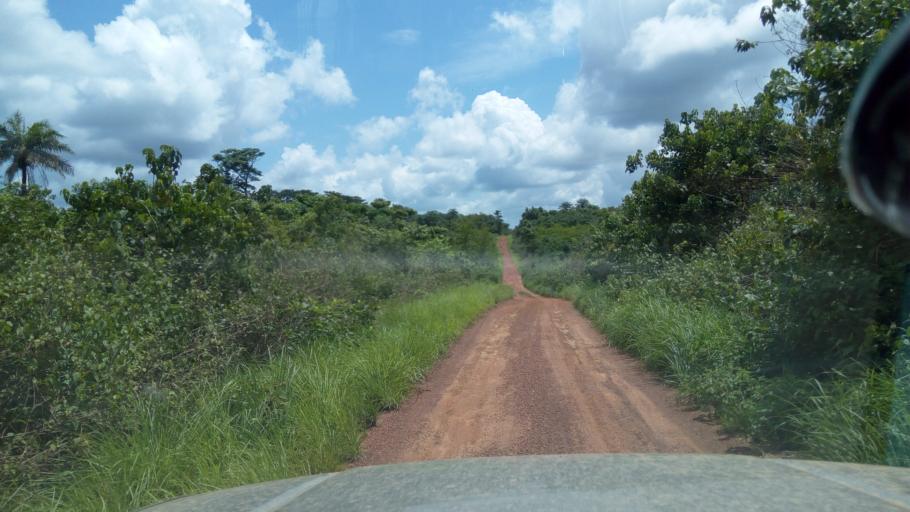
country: SL
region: Southern Province
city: Zimmi
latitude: 7.2845
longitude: -11.2822
